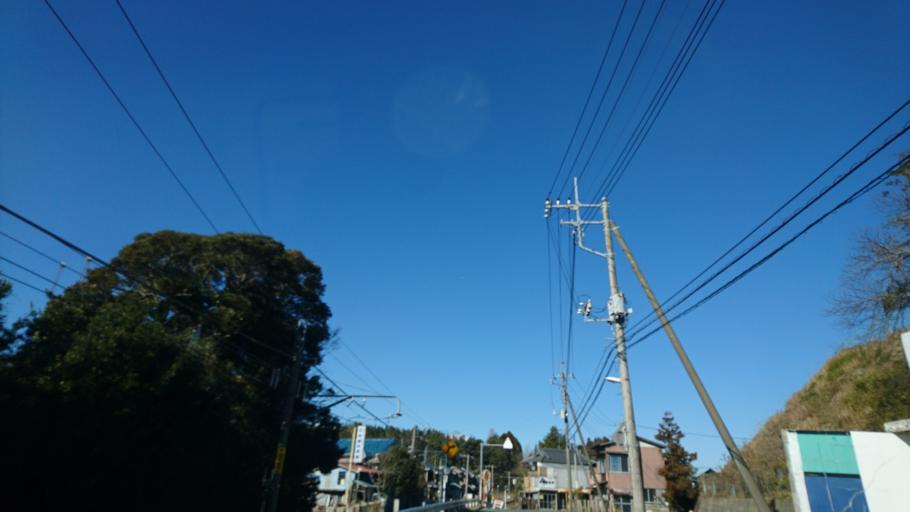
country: JP
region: Chiba
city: Yachimata
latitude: 35.6292
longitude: 140.3612
